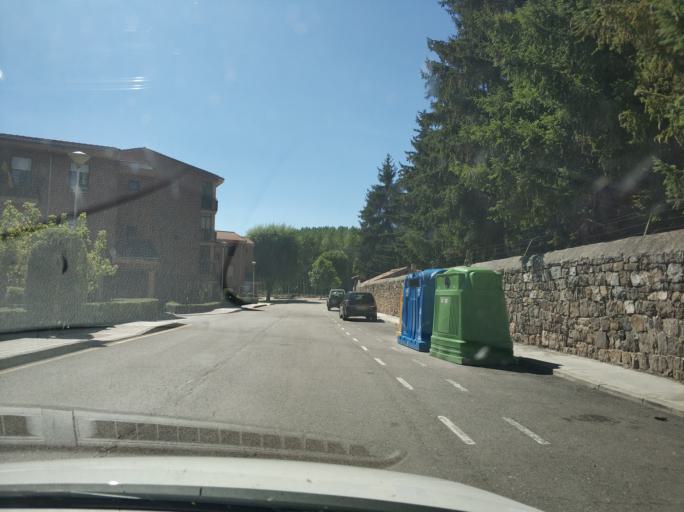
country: ES
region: Castille and Leon
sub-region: Provincia de Palencia
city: Aguilar de Campoo
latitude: 42.7953
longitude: -4.2680
